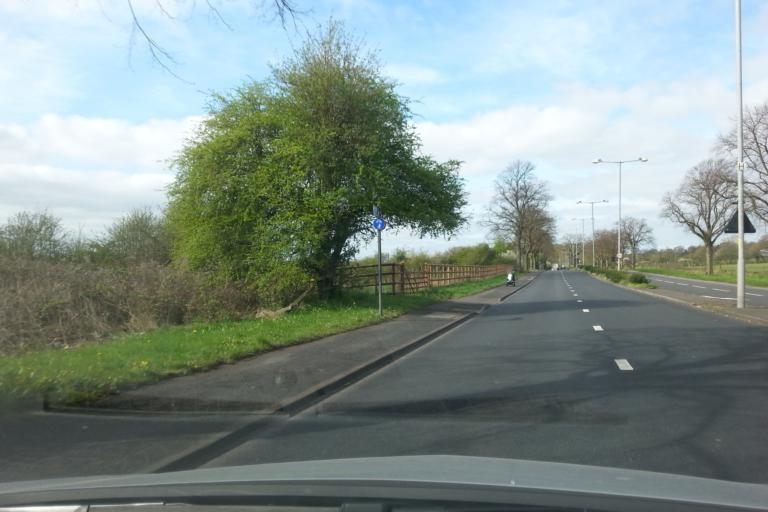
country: GB
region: England
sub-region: Walsall
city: Aldridge
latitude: 52.5907
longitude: -1.9452
